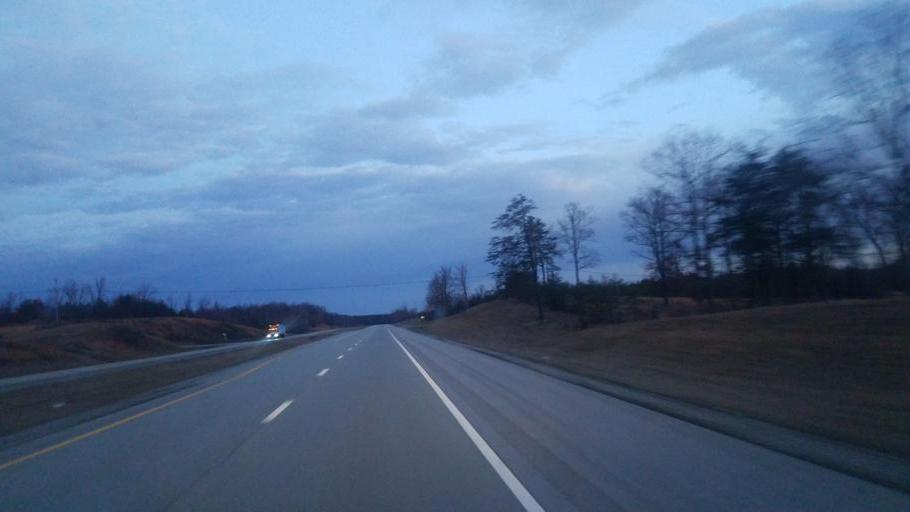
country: US
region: Tennessee
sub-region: Van Buren County
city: Spencer
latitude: 35.6812
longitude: -85.4765
